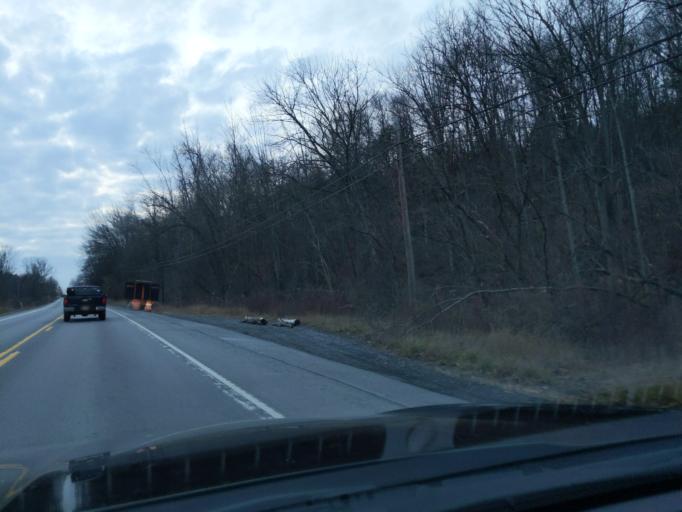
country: US
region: Pennsylvania
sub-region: Blair County
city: Lakemont
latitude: 40.4666
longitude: -78.3042
